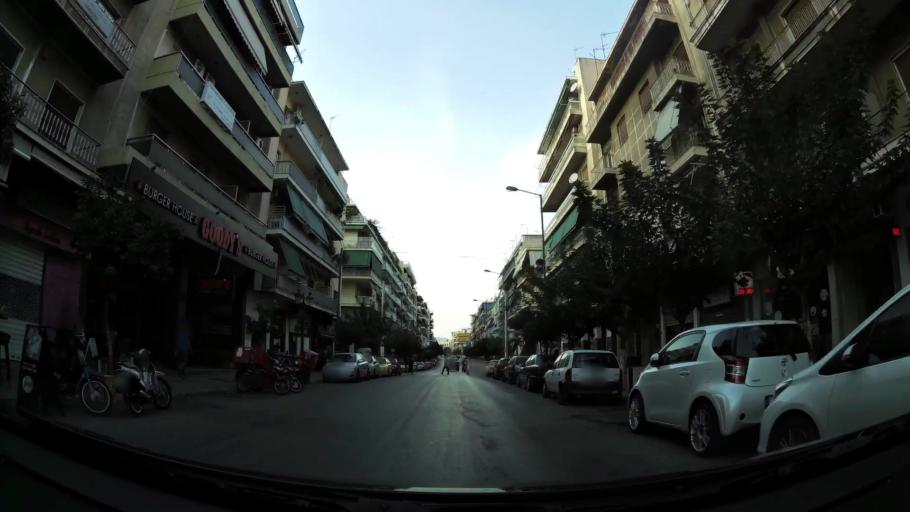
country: GR
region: Attica
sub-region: Nomarchia Athinas
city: Kallithea
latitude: 37.9577
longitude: 23.7001
